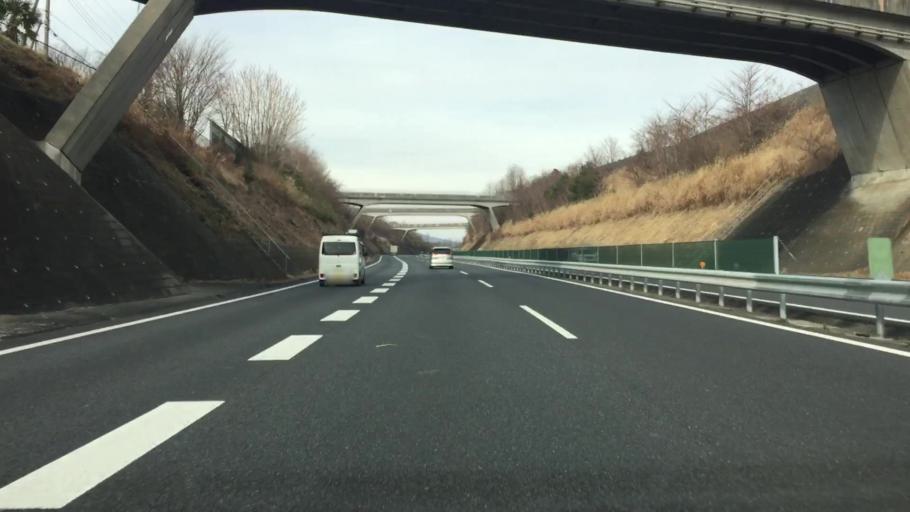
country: JP
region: Gunma
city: Shibukawa
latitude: 36.4932
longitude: 139.0311
